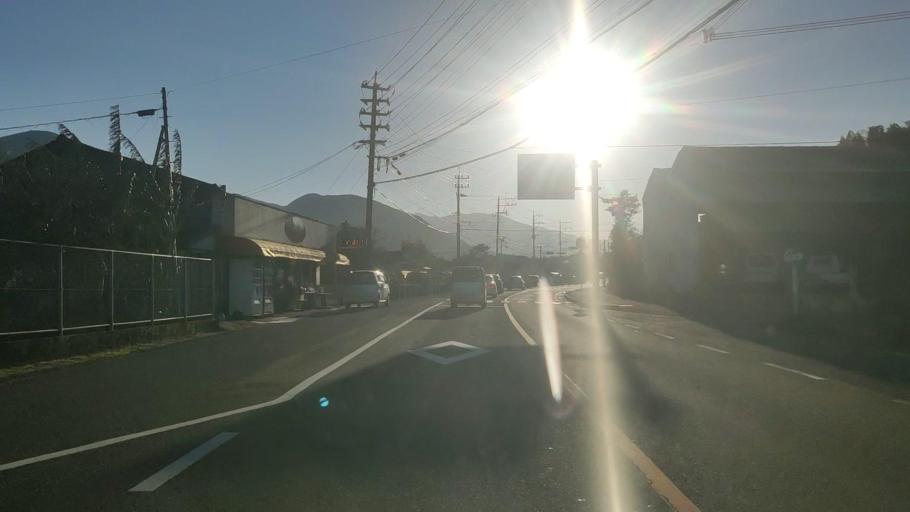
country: JP
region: Miyazaki
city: Miyazaki-shi
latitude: 31.8481
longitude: 131.3499
